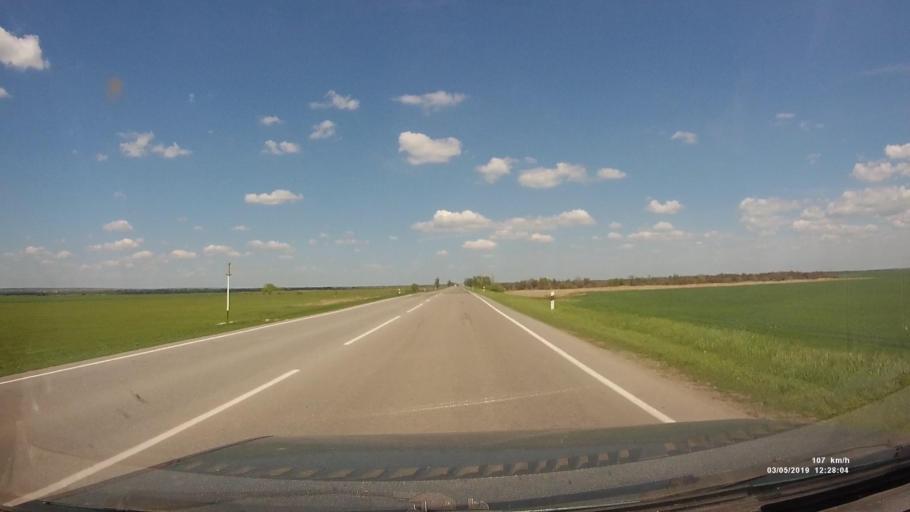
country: RU
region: Rostov
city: Semikarakorsk
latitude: 47.4678
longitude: 40.7254
